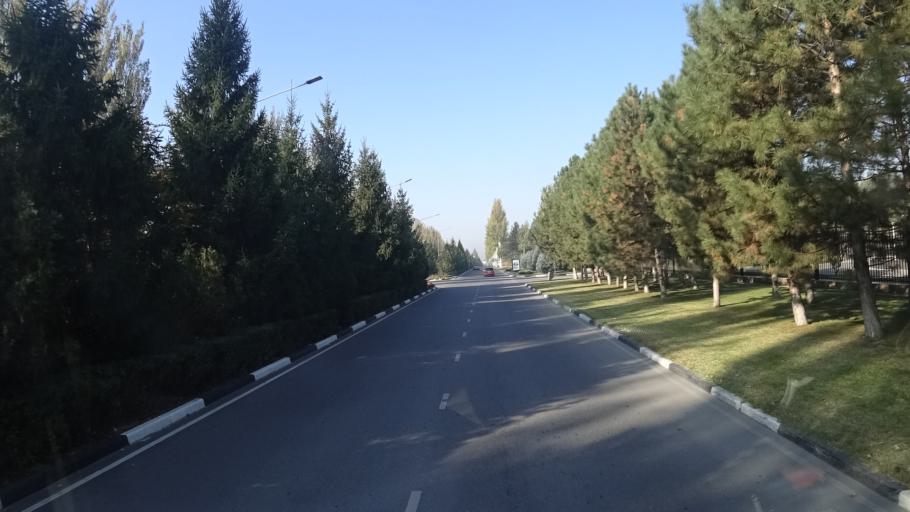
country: KG
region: Chuy
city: Bishkek
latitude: 43.0527
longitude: 74.4646
